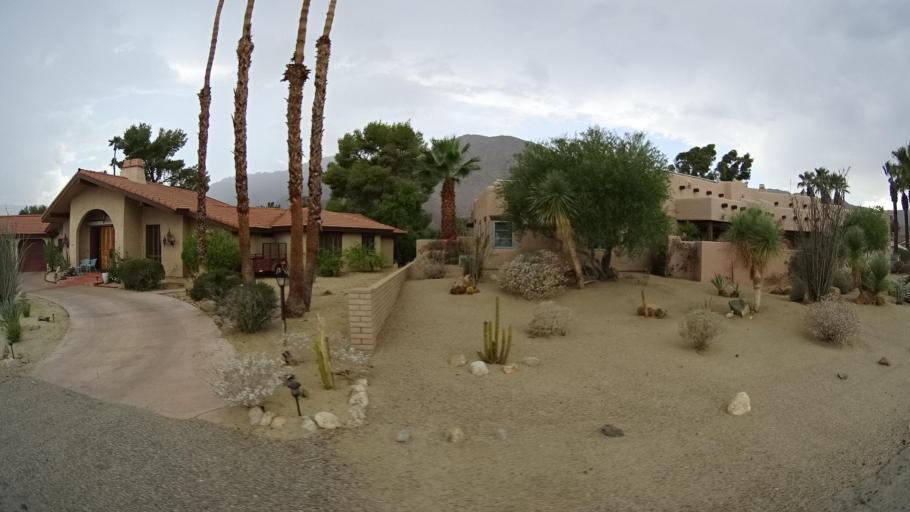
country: US
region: California
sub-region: San Diego County
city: Borrego Springs
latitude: 33.2942
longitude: -116.3858
